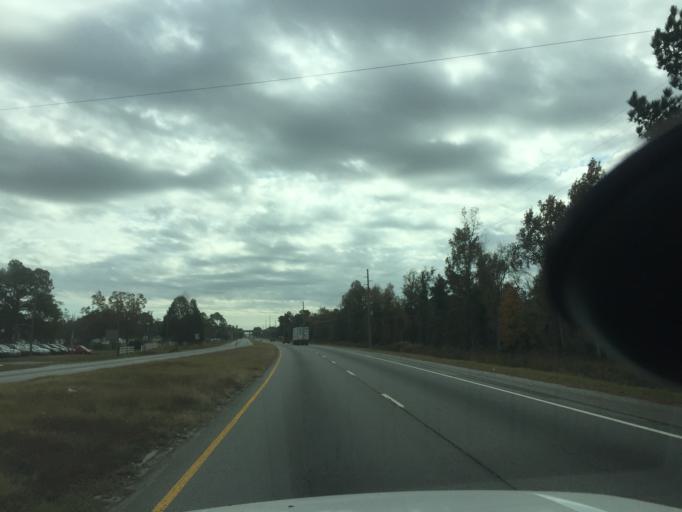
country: US
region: Georgia
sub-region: Chatham County
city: Port Wentworth
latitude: 32.1701
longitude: -81.1869
